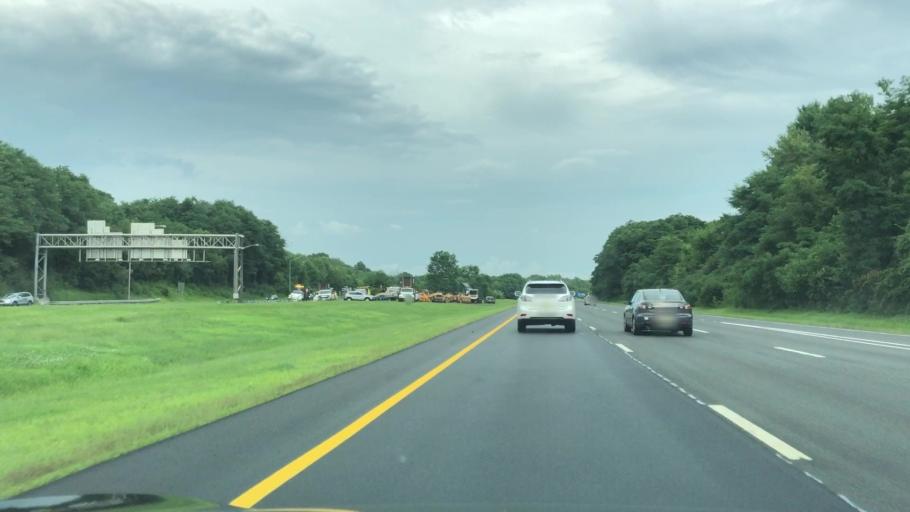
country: US
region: New Jersey
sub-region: Mercer County
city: Ewing
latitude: 40.2912
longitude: -74.7796
